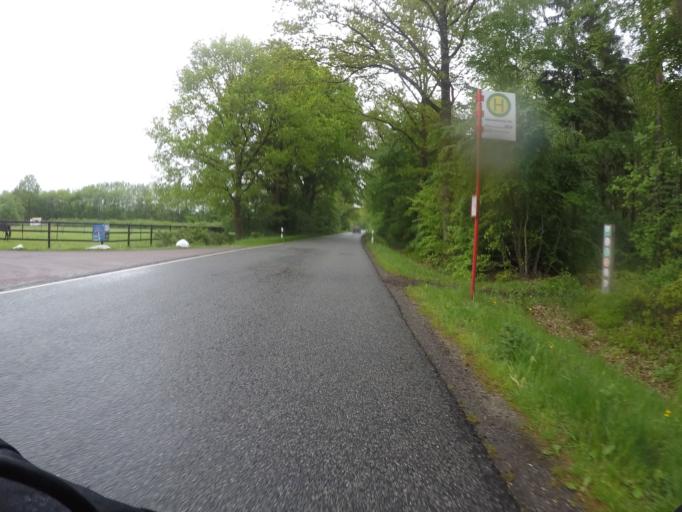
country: DE
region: Schleswig-Holstein
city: Heidmuhlen
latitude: 53.9653
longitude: 10.1250
